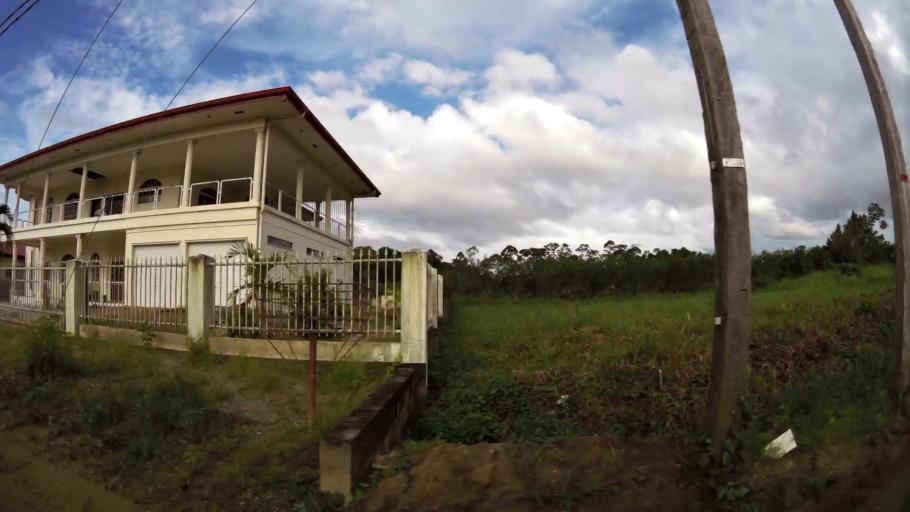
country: SR
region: Paramaribo
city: Paramaribo
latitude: 5.8538
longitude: -55.2313
